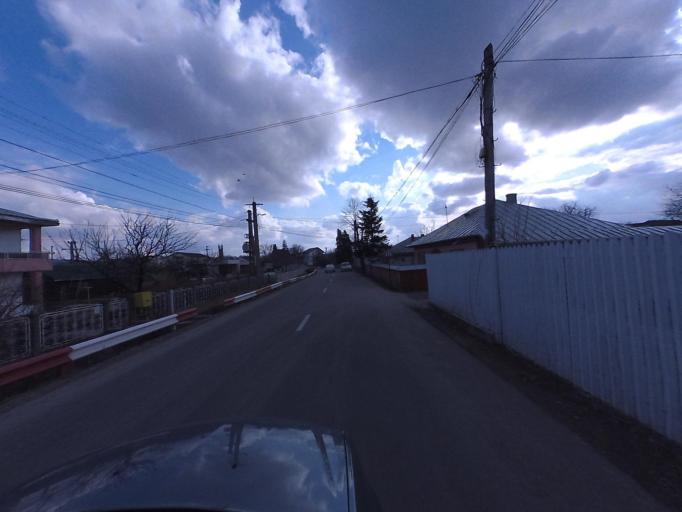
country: RO
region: Neamt
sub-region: Oras Targu Neamt
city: Targu Neamt
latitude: 47.2079
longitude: 26.3739
